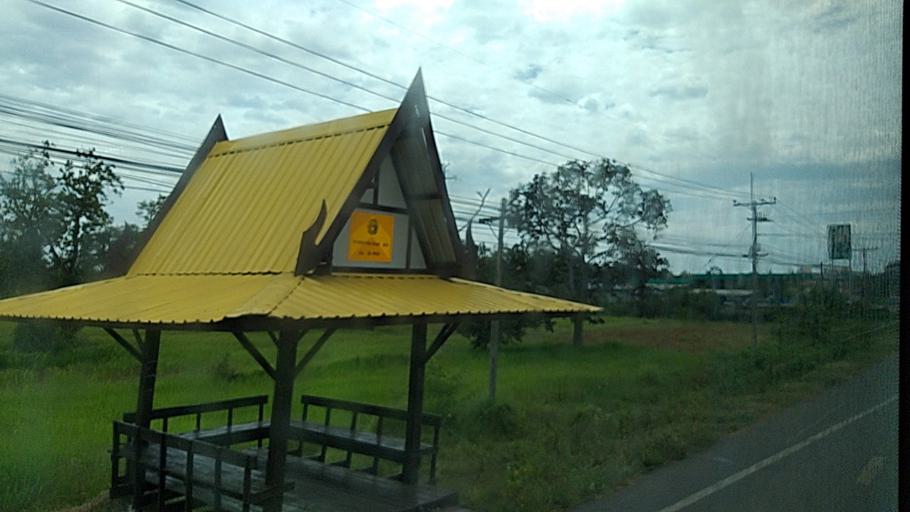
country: TH
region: Maha Sarakham
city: Kantharawichai
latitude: 16.2943
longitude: 103.2958
